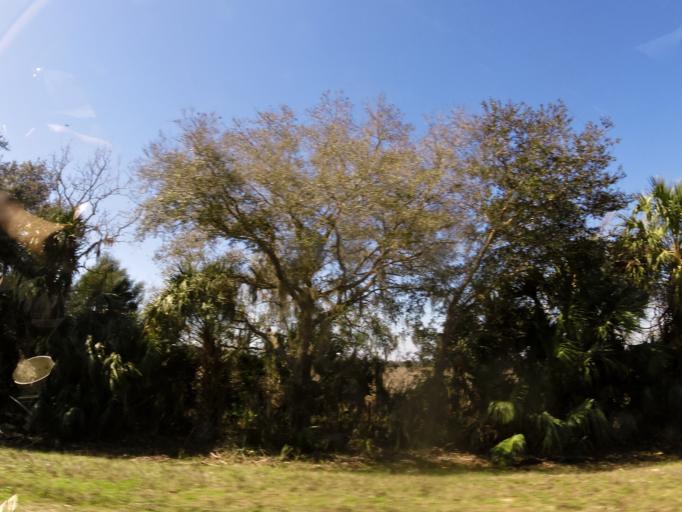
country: US
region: Florida
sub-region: Levy County
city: Inglis
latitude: 29.0951
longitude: -82.6361
